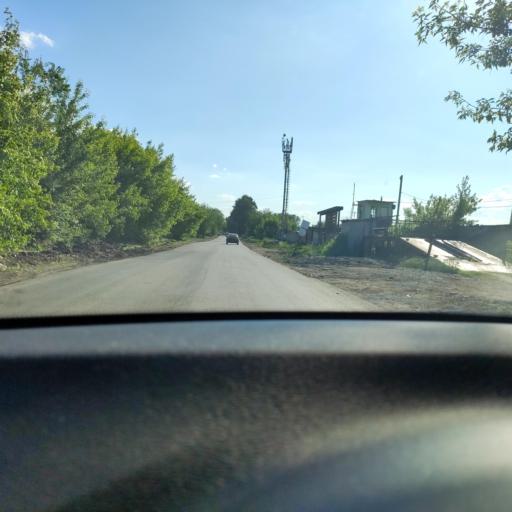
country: RU
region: Samara
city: Smyshlyayevka
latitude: 53.2444
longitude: 50.3607
